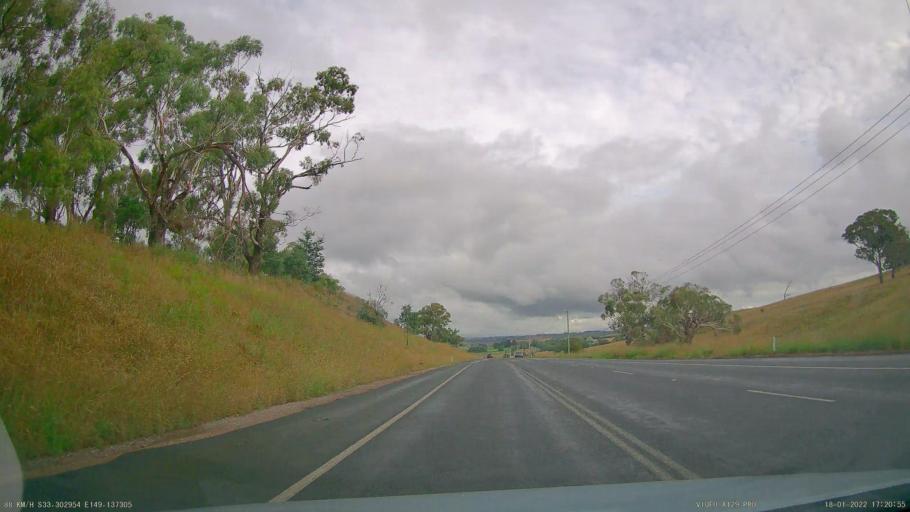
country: AU
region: New South Wales
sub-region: Orange Municipality
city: Orange
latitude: -33.3031
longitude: 149.1374
